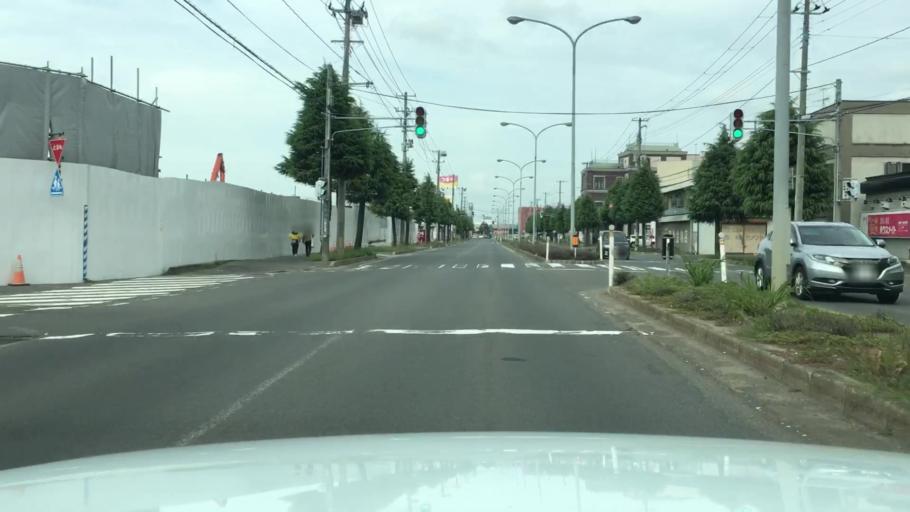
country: JP
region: Aomori
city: Hirosaki
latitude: 40.6067
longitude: 140.4789
